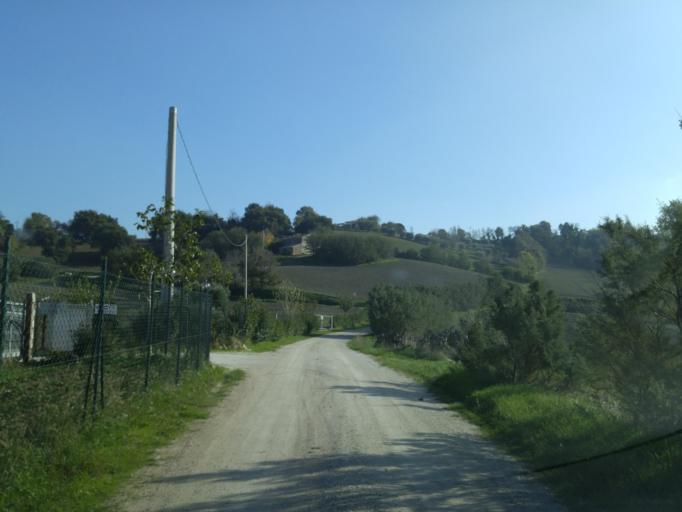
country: IT
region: The Marches
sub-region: Provincia di Pesaro e Urbino
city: Piagge
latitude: 43.7302
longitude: 12.9566
